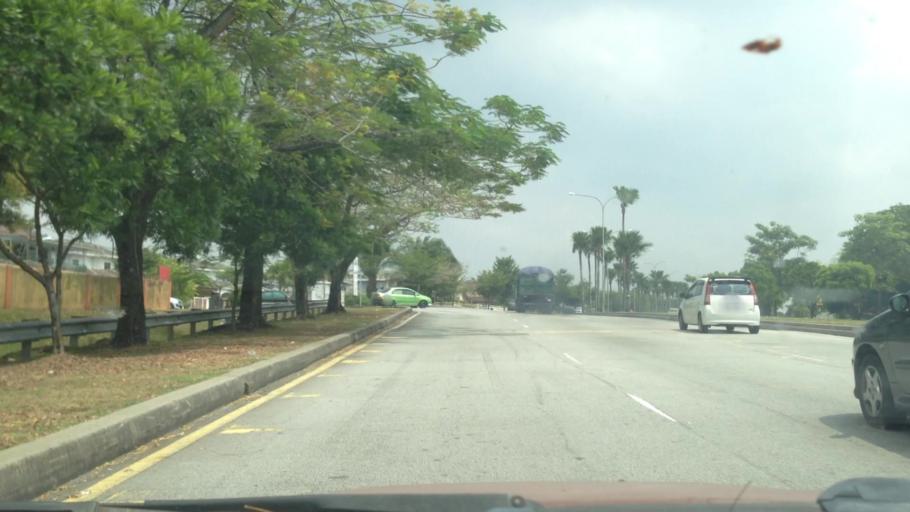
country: MY
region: Selangor
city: Subang Jaya
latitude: 3.0393
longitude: 101.5801
